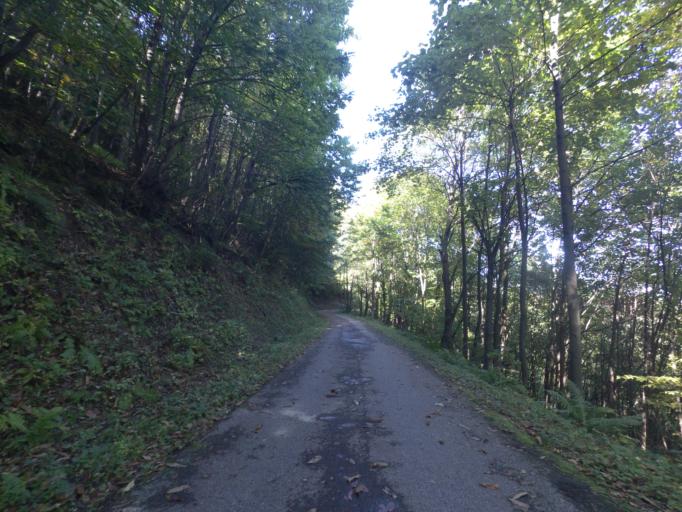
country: AT
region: Styria
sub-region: Politischer Bezirk Leibnitz
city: Kitzeck im Sausal
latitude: 46.7831
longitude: 15.4333
